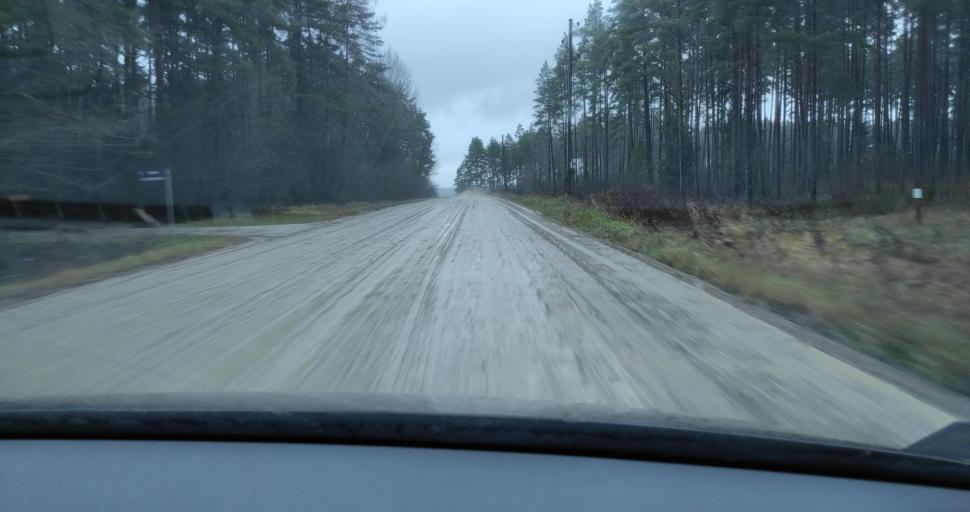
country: LV
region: Skrunda
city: Skrunda
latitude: 56.6860
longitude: 22.2221
